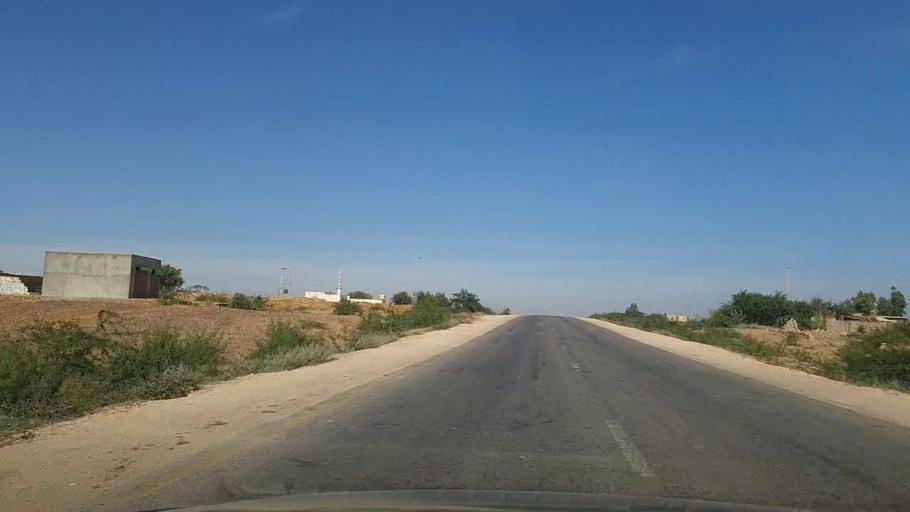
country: PK
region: Sindh
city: Kotri
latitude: 25.1836
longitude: 68.2401
